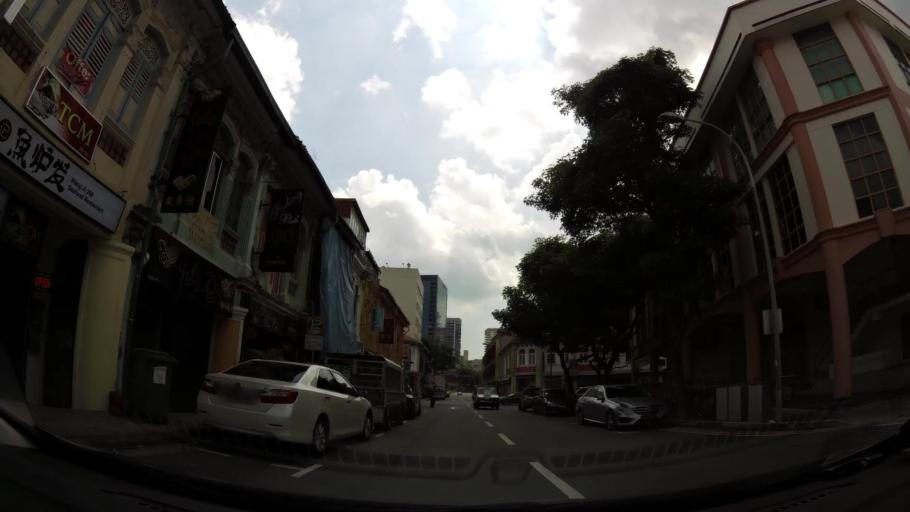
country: SG
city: Singapore
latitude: 1.3076
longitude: 103.8578
